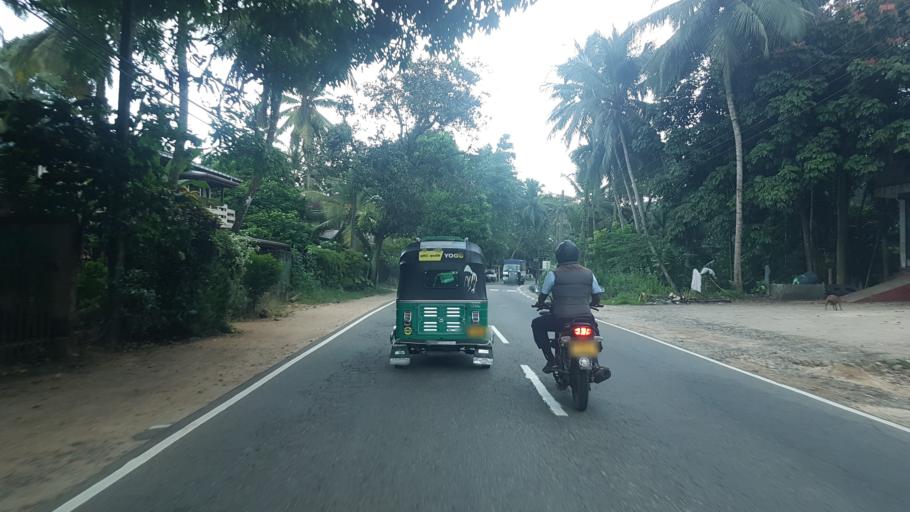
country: LK
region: Western
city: Hanwella Ihala
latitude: 7.0093
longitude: 80.2618
